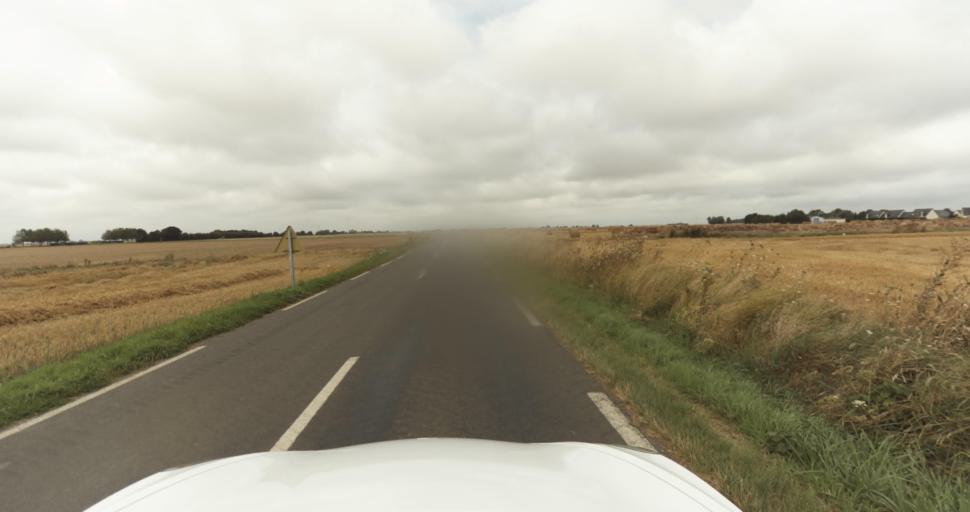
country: FR
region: Haute-Normandie
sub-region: Departement de l'Eure
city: Claville
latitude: 49.0741
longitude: 1.0648
